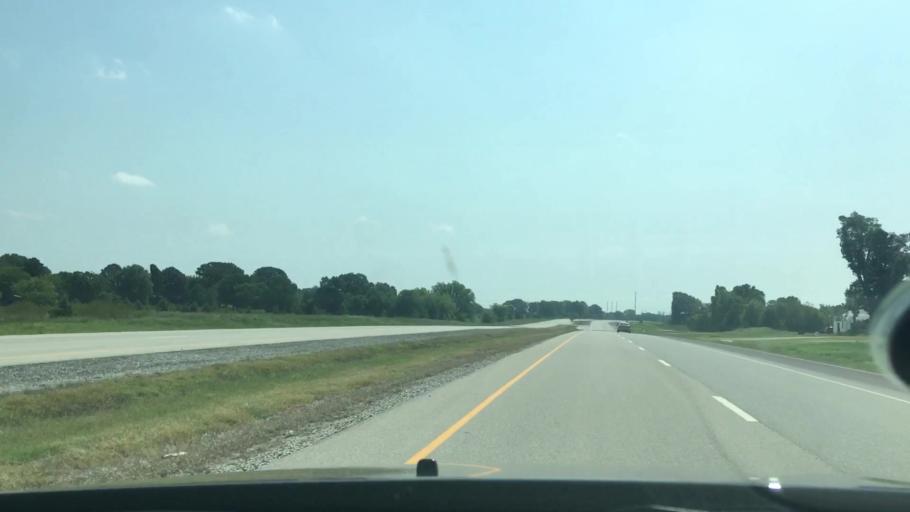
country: US
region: Oklahoma
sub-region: Atoka County
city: Atoka
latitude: 34.3381
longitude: -96.0618
